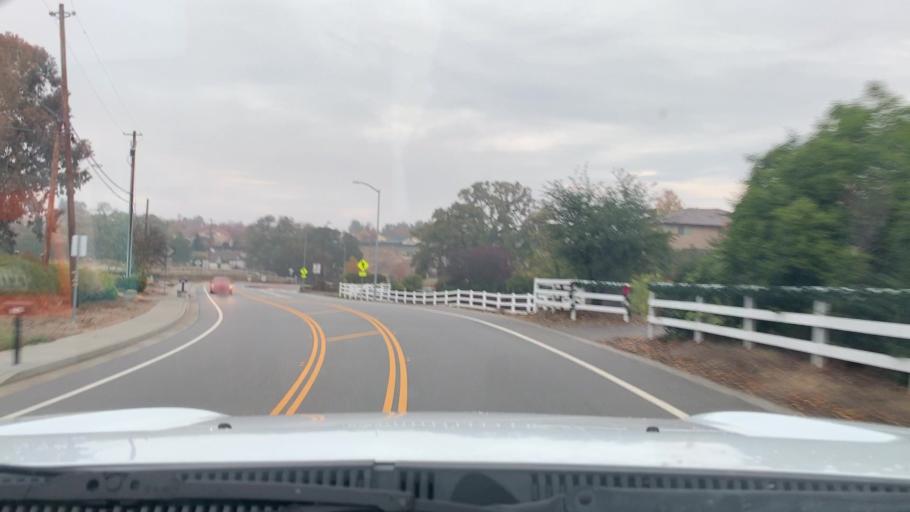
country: US
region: California
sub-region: San Luis Obispo County
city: Paso Robles
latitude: 35.6365
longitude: -120.6633
